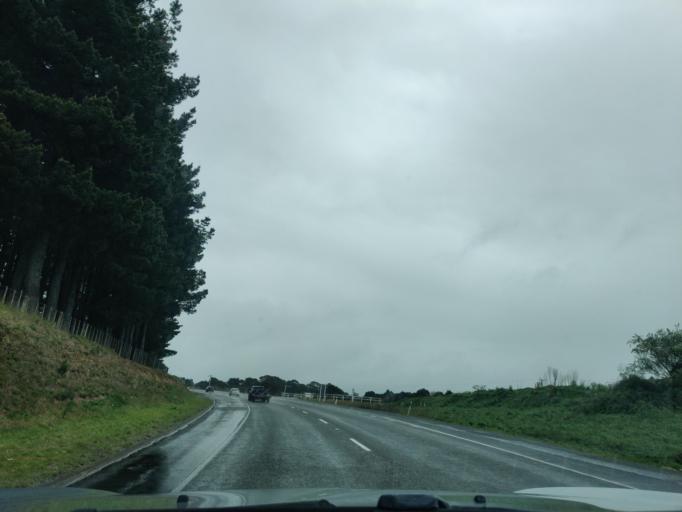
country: NZ
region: Manawatu-Wanganui
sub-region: Palmerston North City
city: Palmerston North
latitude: -40.0546
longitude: 176.2332
